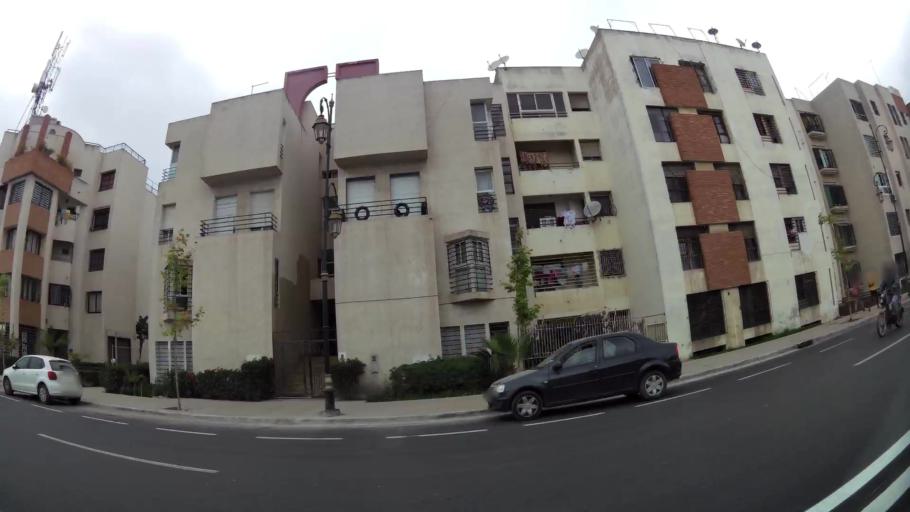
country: MA
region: Rabat-Sale-Zemmour-Zaer
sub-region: Rabat
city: Rabat
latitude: 33.9780
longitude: -6.8159
